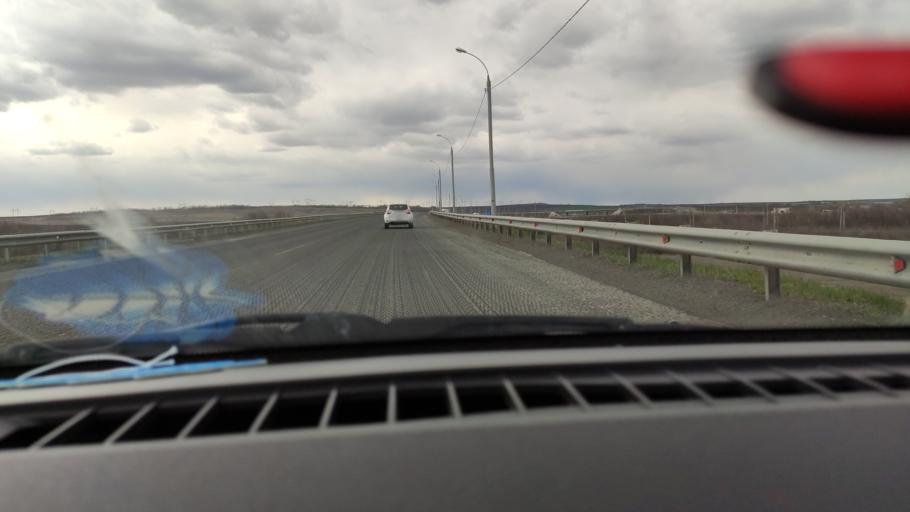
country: RU
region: Saratov
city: Yelshanka
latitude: 51.7992
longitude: 46.1847
